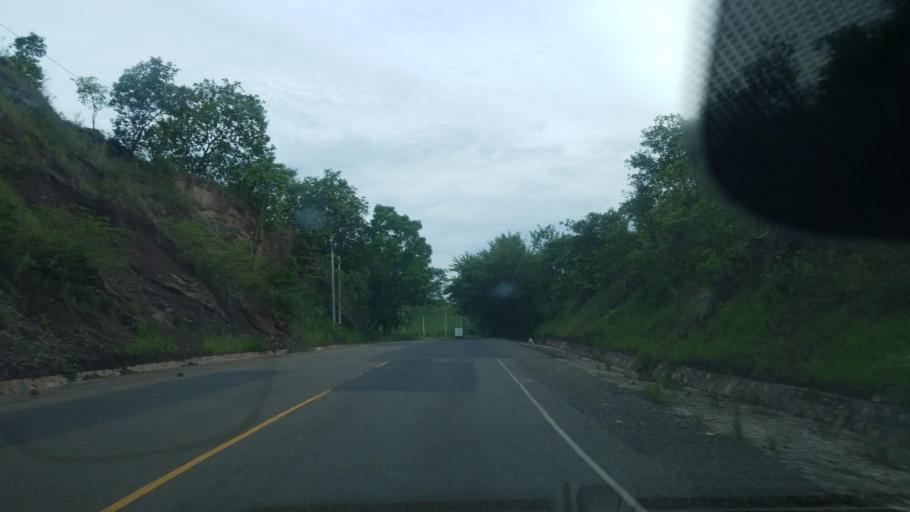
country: HN
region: Santa Barbara
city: Concepcion del Sur
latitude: 14.8145
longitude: -88.1772
